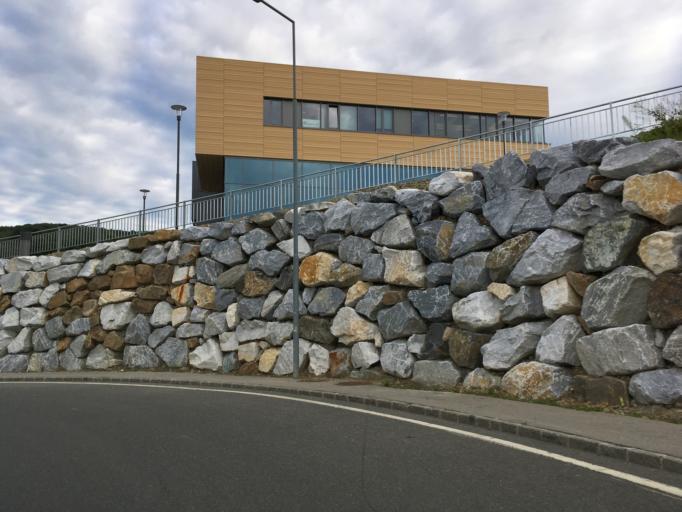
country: AT
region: Lower Austria
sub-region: Politischer Bezirk Tulln
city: Wordern
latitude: 48.3092
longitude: 16.2567
